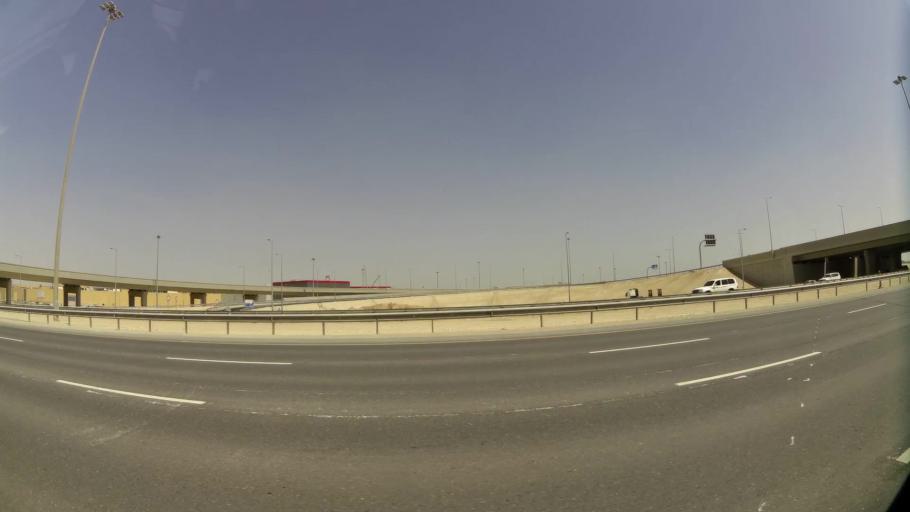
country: QA
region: Baladiyat Umm Salal
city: Umm Salal Muhammad
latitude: 25.3798
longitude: 51.4399
